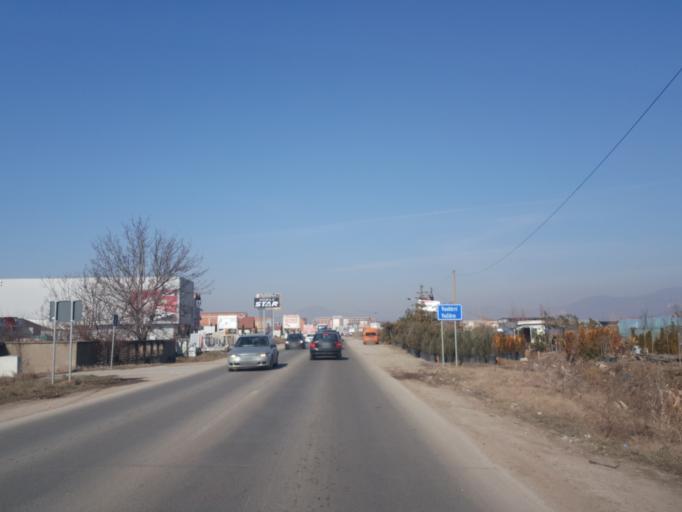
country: XK
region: Mitrovica
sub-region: Vushtrri
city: Vushtrri
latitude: 42.8102
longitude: 20.9870
